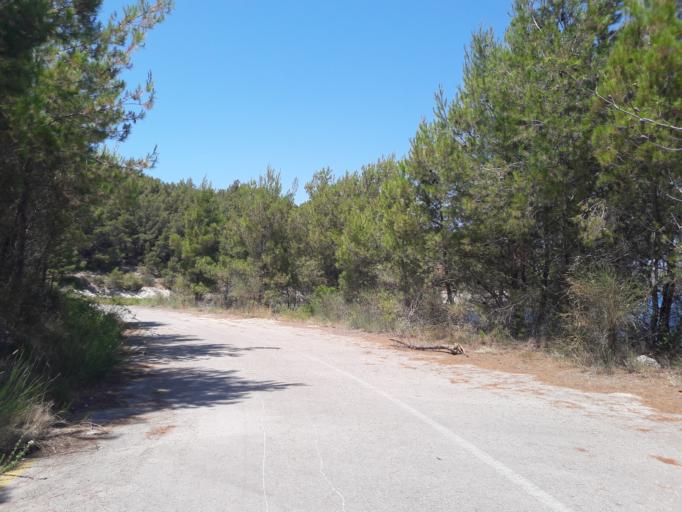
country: HR
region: Sibensko-Kniniska
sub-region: Grad Sibenik
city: Sibenik
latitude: 43.7029
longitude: 15.8466
